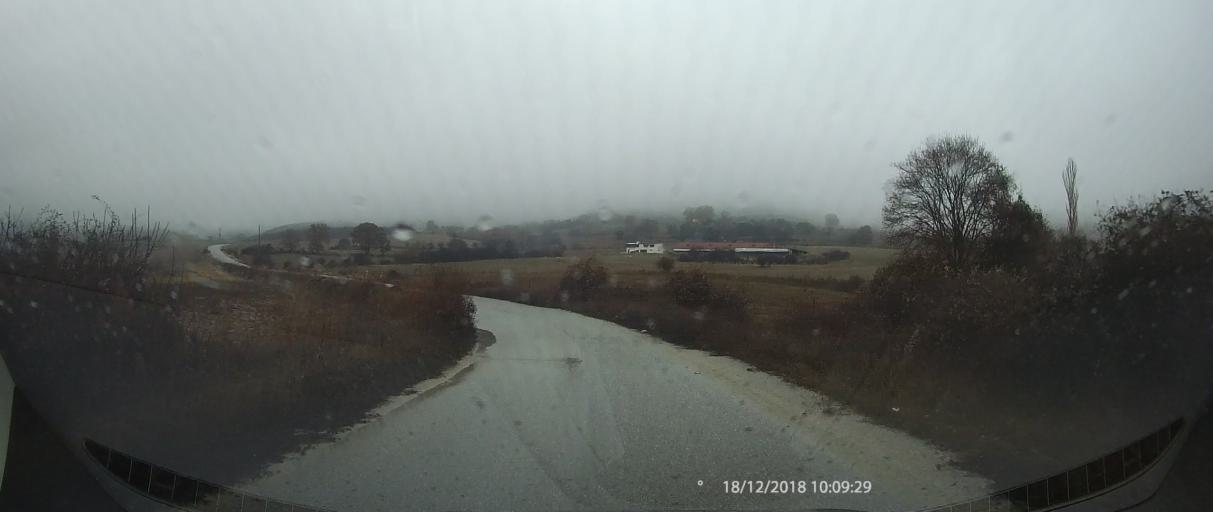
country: GR
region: Thessaly
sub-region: Nomos Larisis
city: Livadi
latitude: 40.0815
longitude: 22.2153
